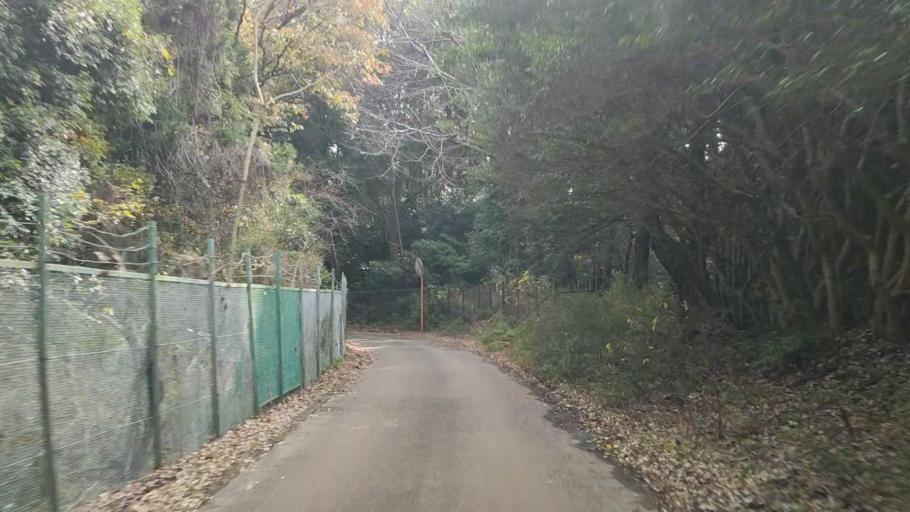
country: JP
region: Kanagawa
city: Minami-rinkan
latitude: 35.4843
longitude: 139.4978
